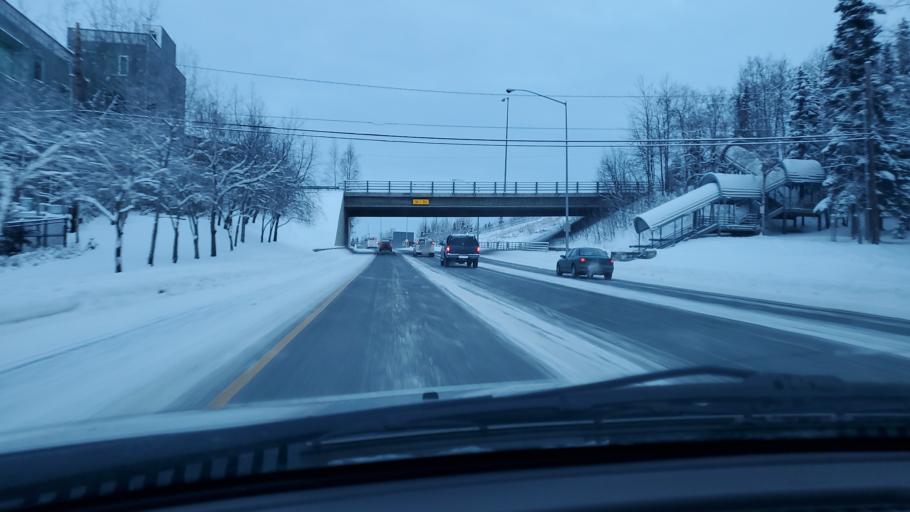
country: US
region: Alaska
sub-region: Anchorage Municipality
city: Anchorage
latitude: 61.2069
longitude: -149.8832
